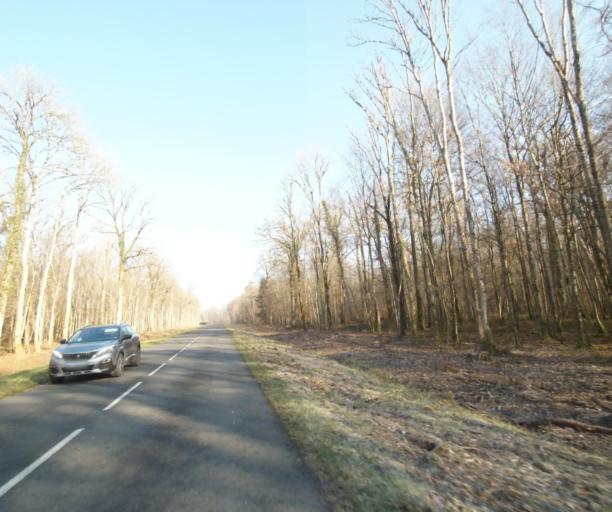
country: FR
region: Champagne-Ardenne
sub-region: Departement de la Haute-Marne
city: Wassy
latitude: 48.4781
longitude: 4.9303
